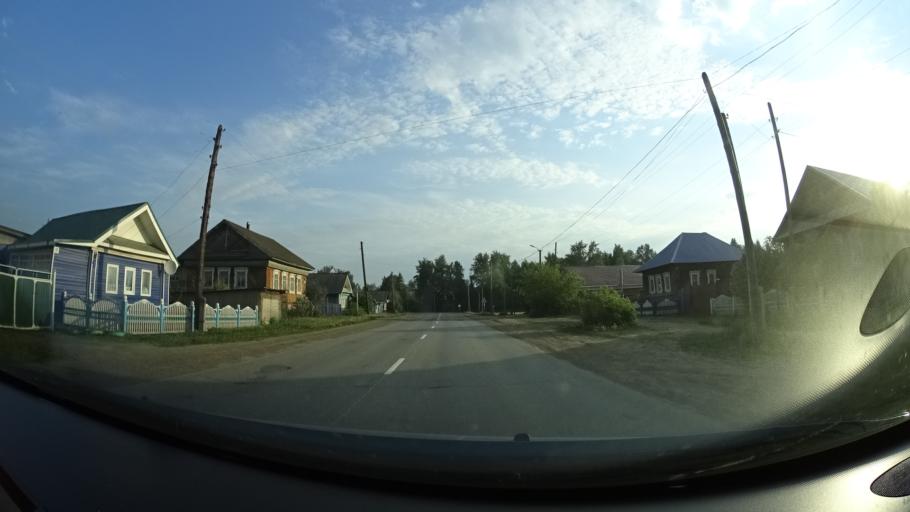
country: RU
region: Perm
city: Barda
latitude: 56.9335
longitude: 55.5926
